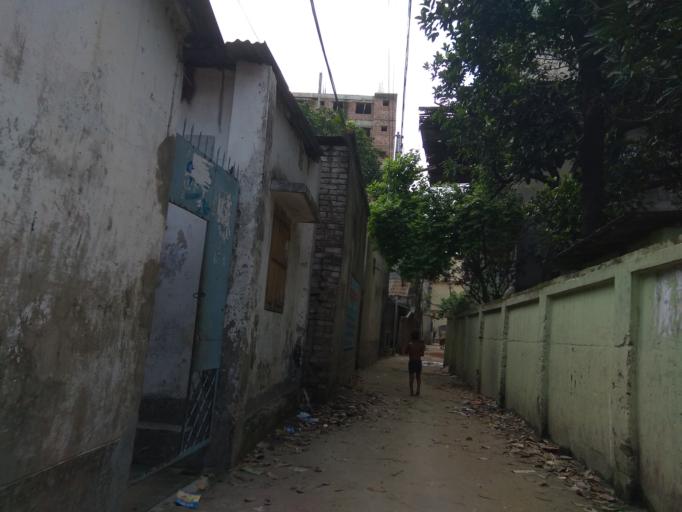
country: BD
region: Dhaka
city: Tungi
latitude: 23.8221
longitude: 90.3911
